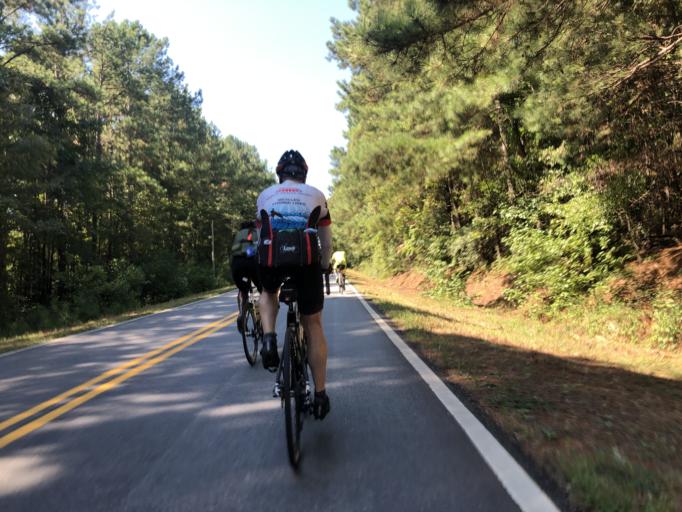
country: US
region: Georgia
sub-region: Coweta County
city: Newnan
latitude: 33.4010
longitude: -84.9578
